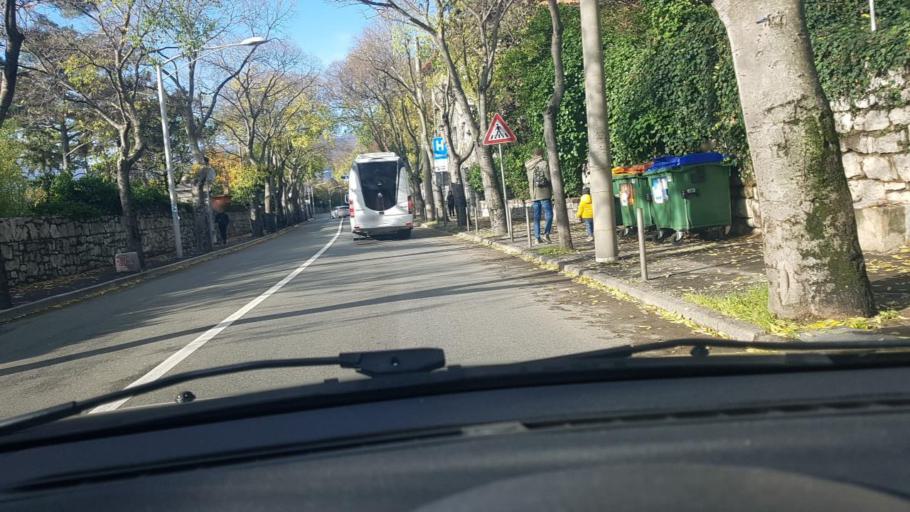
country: HR
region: Primorsko-Goranska
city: Marinici
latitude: 45.3420
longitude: 14.3708
